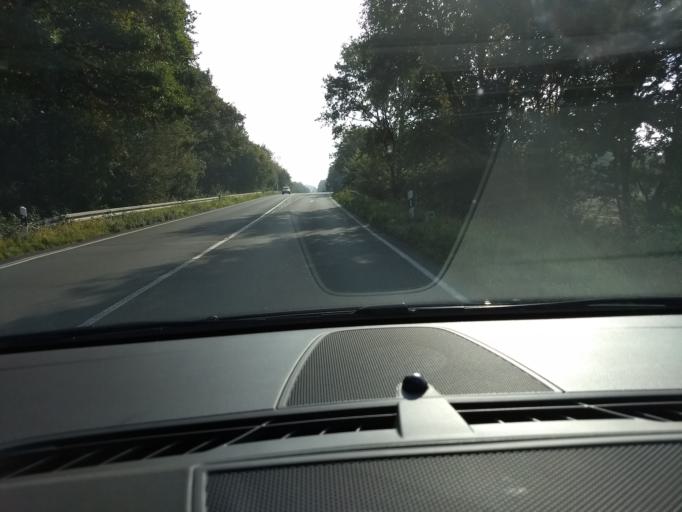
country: DE
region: North Rhine-Westphalia
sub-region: Regierungsbezirk Munster
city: Heiden
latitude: 51.8087
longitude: 6.9802
